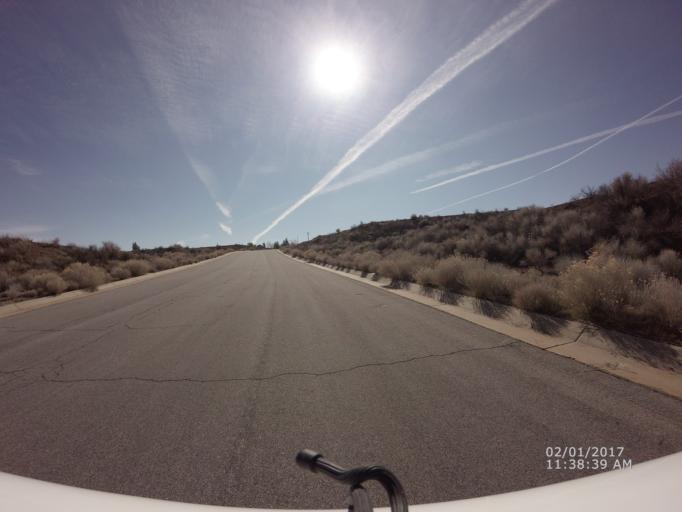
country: US
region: California
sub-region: Los Angeles County
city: Palmdale
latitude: 34.5436
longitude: -118.1163
